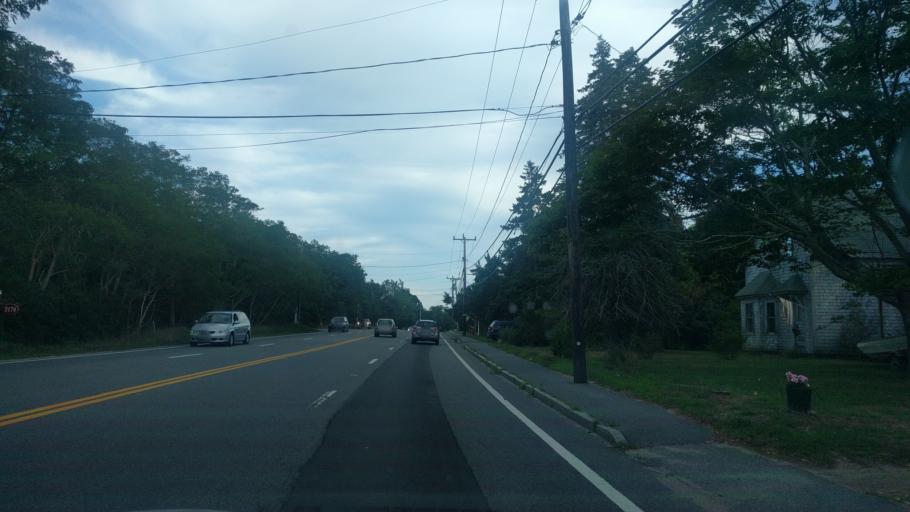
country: US
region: Massachusetts
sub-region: Barnstable County
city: Eastham
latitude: 41.8256
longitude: -69.9716
